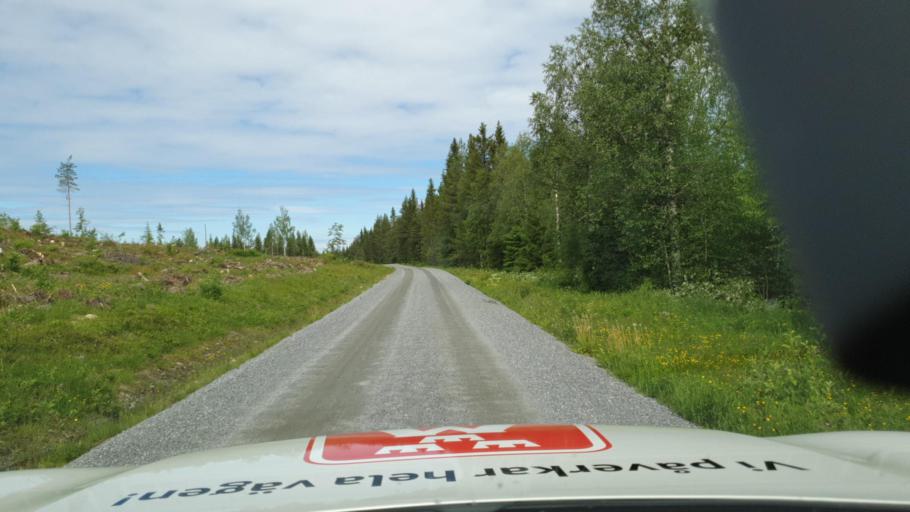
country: SE
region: Vaesterbotten
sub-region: Skelleftea Kommun
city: Langsele
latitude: 64.6236
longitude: 20.2594
